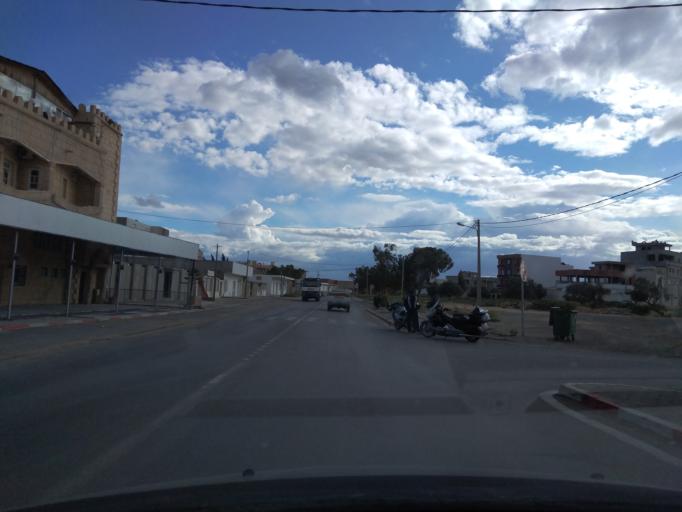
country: TN
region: Susah
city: Masakin
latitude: 35.7190
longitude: 10.5644
